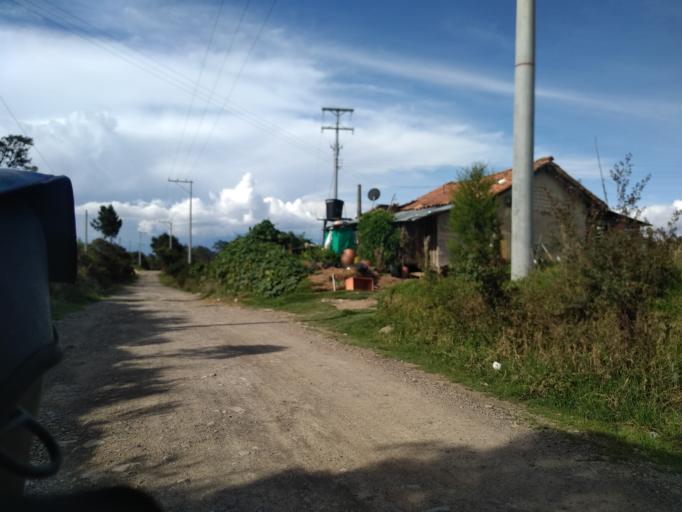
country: CO
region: Boyaca
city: Raquira
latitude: 5.4687
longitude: -73.6374
